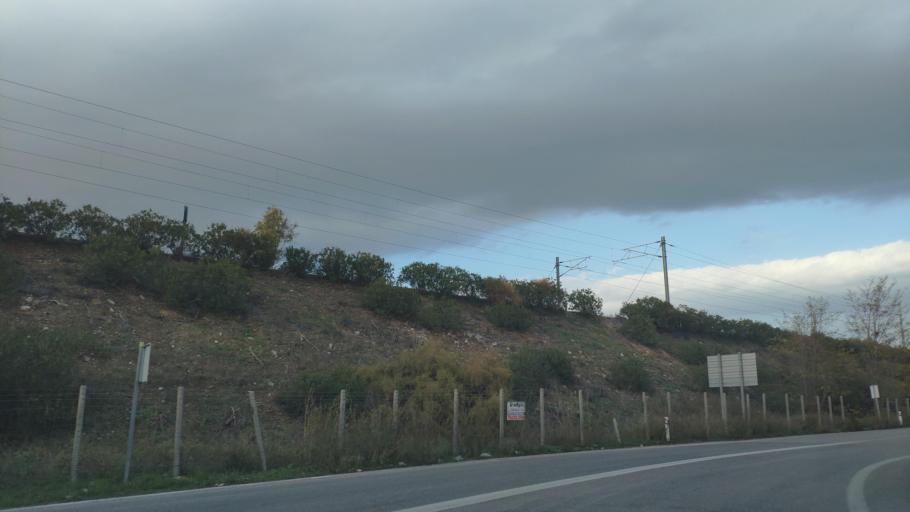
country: GR
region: Attica
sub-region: Nomarchia Dytikis Attikis
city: Megara
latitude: 37.9997
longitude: 23.3753
